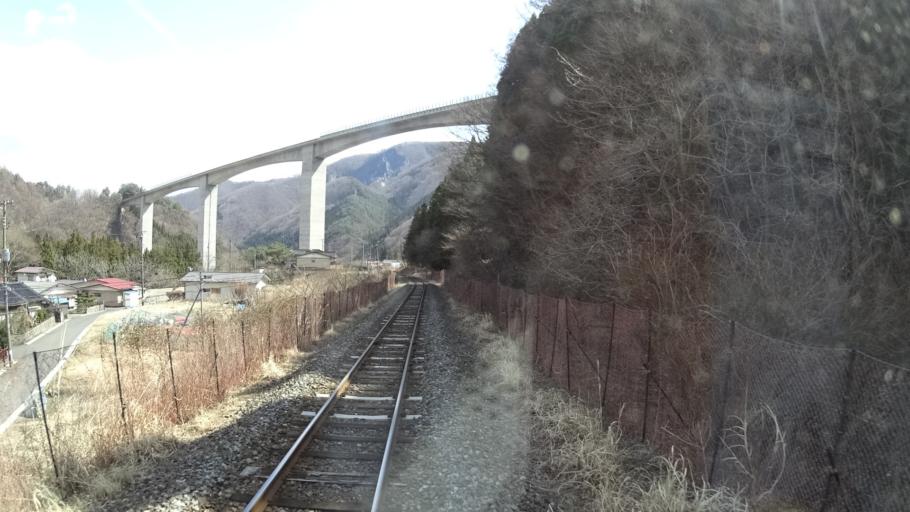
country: JP
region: Iwate
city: Kamaishi
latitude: 39.2530
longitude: 141.7524
